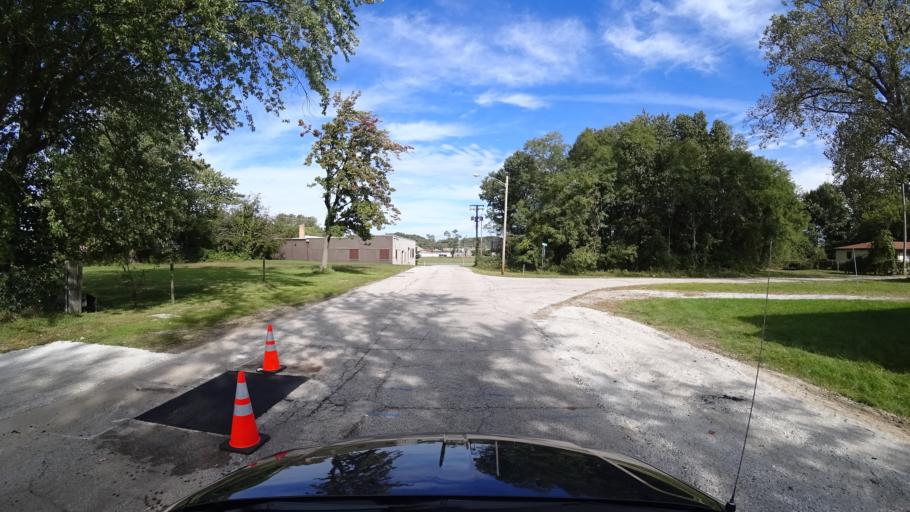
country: US
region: Indiana
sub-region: LaPorte County
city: Michigan City
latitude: 41.7212
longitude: -86.8877
